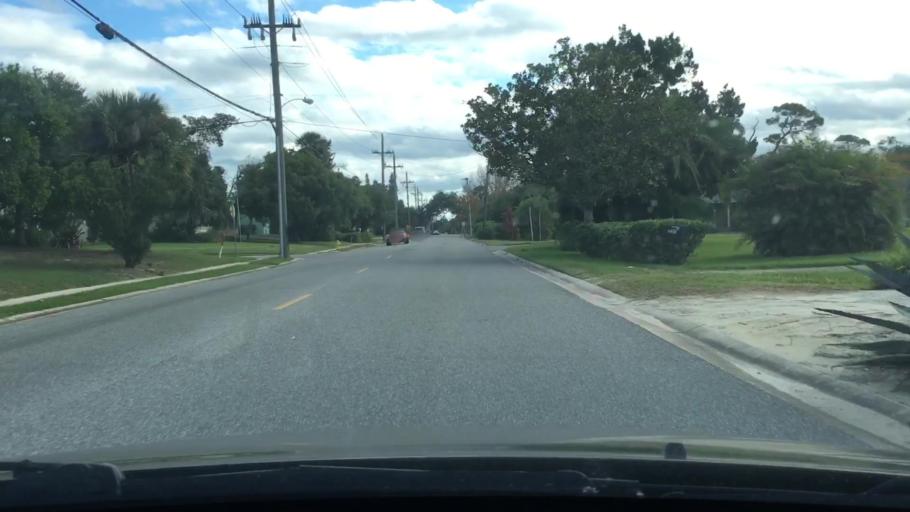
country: US
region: Florida
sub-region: Volusia County
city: Ormond Beach
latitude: 29.2834
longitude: -81.0424
